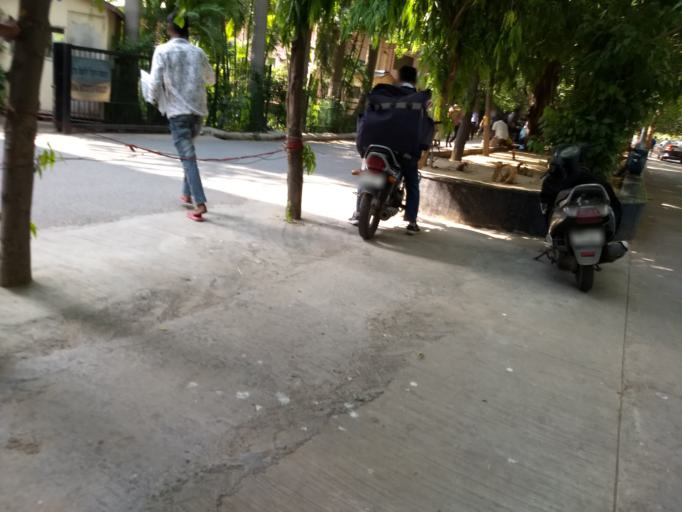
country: IN
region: NCT
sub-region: New Delhi
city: New Delhi
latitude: 28.5668
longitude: 77.2030
